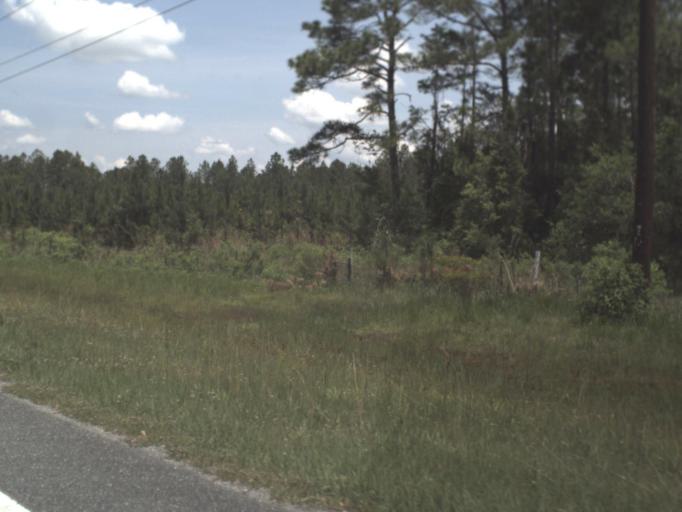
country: US
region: Florida
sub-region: Bradford County
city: Starke
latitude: 29.9736
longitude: -82.2170
